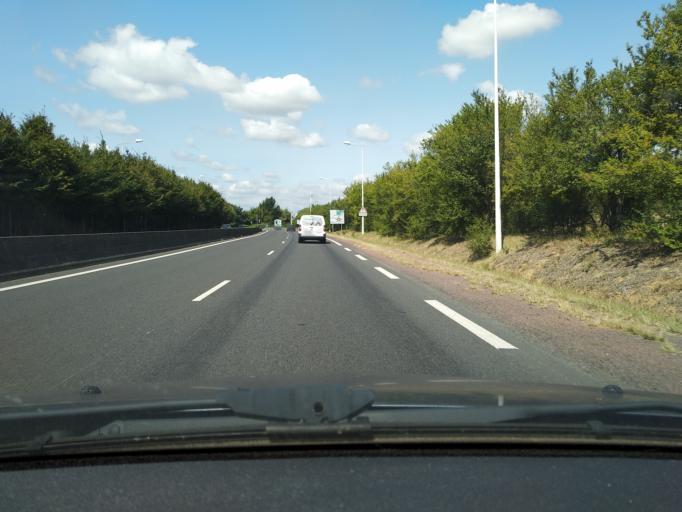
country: FR
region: Centre
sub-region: Departement d'Indre-et-Loire
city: Parcay-Meslay
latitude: 47.4233
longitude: 0.7140
